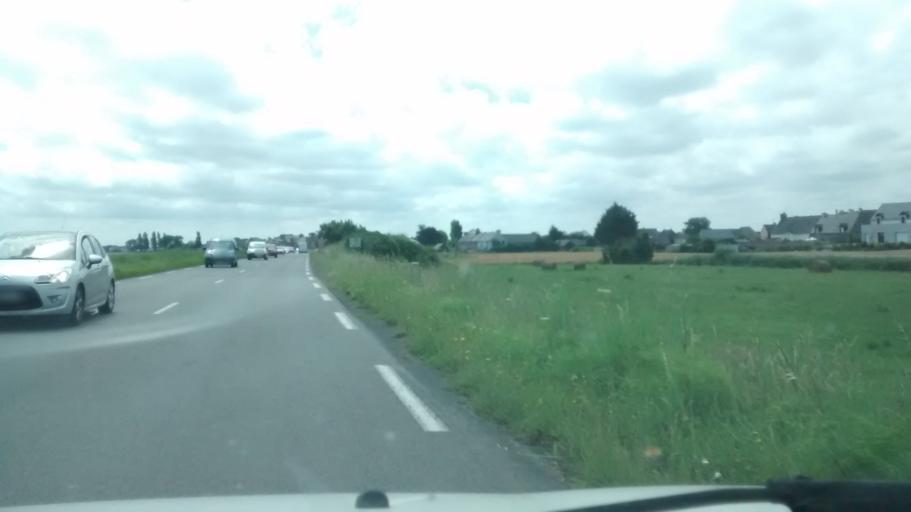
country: FR
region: Brittany
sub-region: Departement d'Ille-et-Vilaine
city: La Fresnais
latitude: 48.6268
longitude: -1.8599
